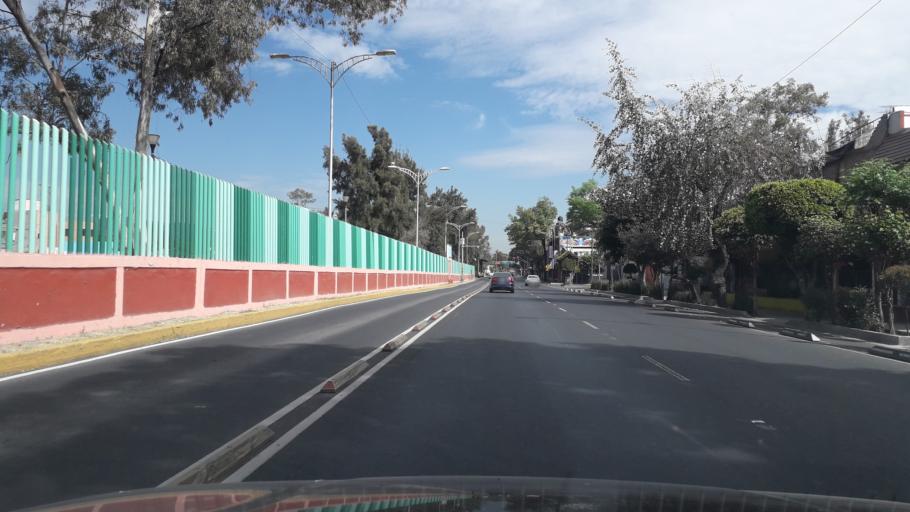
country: MX
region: Mexico City
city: Gustavo A. Madero
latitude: 19.4989
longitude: -99.0891
